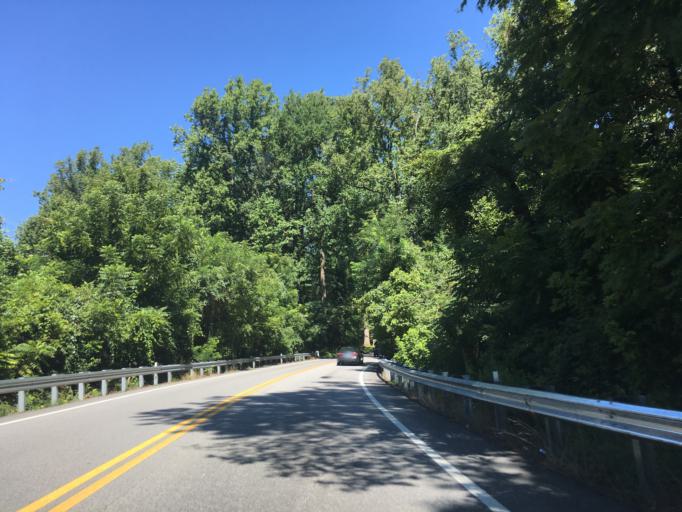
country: US
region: Maryland
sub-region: Anne Arundel County
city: Crownsville
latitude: 39.0440
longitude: -76.6088
